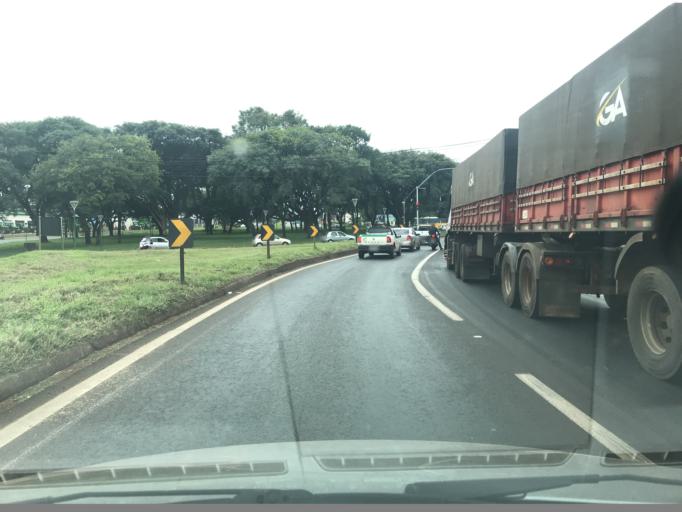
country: BR
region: Parana
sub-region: Maringa
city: Maringa
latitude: -23.4234
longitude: -51.9746
